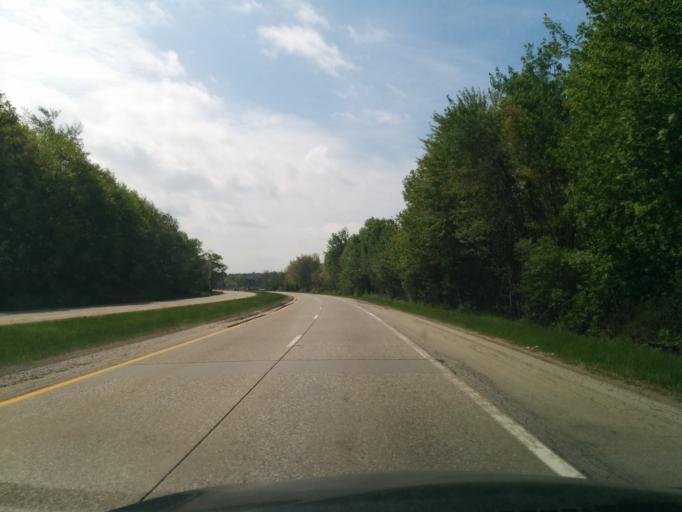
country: US
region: Michigan
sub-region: Ottawa County
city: Grand Haven
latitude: 43.0350
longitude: -86.2204
